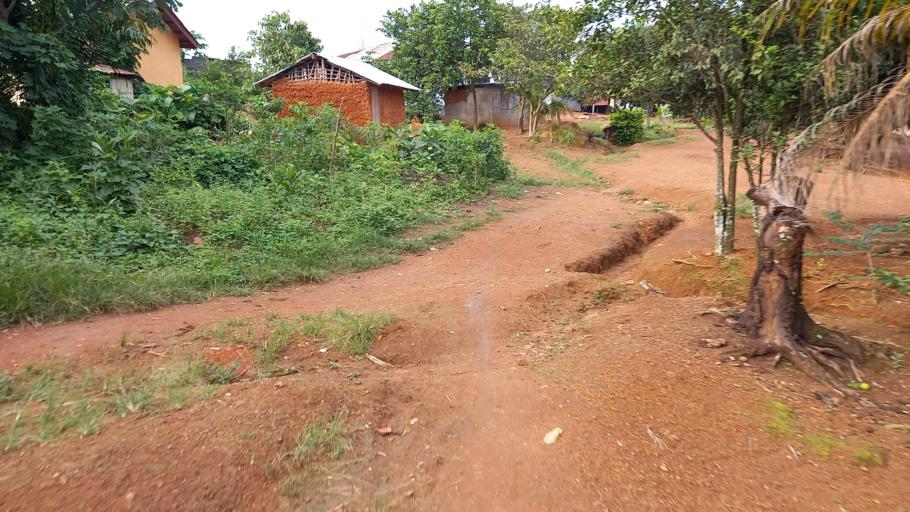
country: SL
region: Eastern Province
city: Kailahun
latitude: 8.2695
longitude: -10.5802
